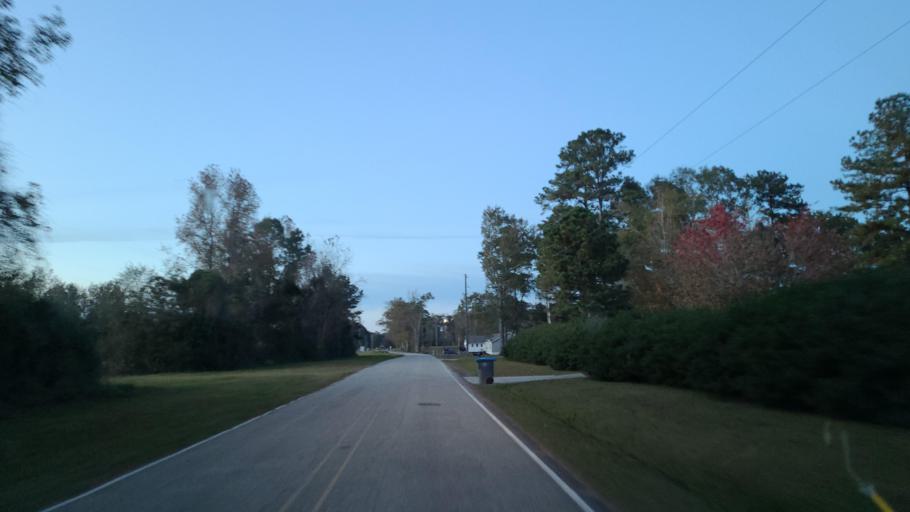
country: US
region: Mississippi
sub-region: Perry County
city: New Augusta
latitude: 31.1589
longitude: -89.2115
